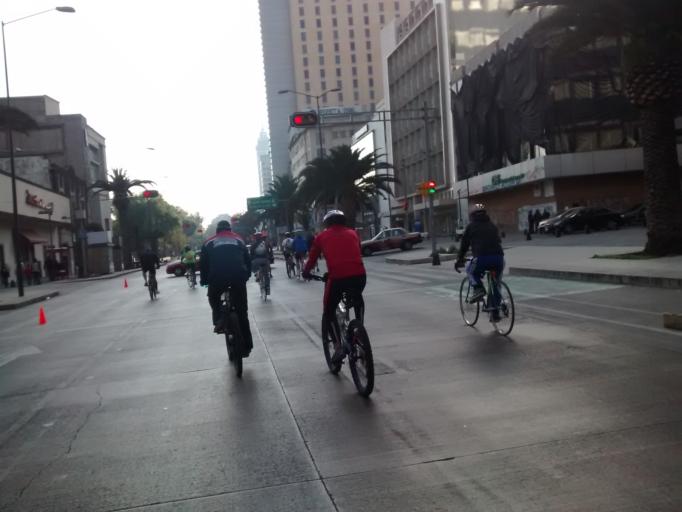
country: MX
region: Mexico City
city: Cuauhtemoc
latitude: 19.4352
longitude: -99.1484
